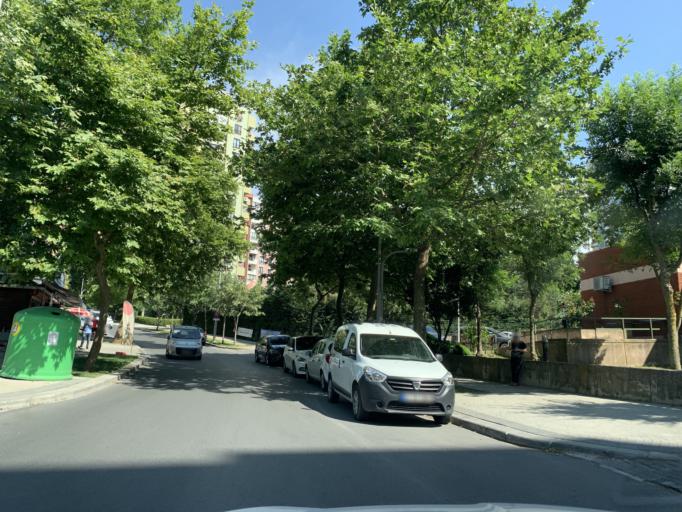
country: TR
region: Istanbul
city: Esenyurt
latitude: 41.0665
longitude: 28.6782
